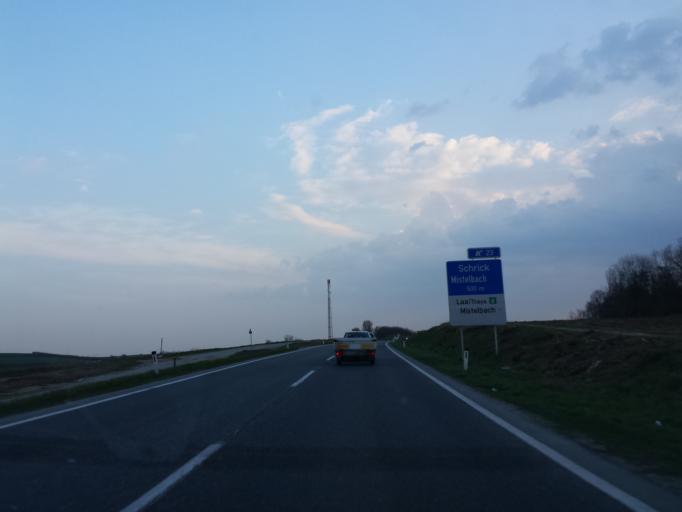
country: AT
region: Lower Austria
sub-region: Politischer Bezirk Mistelbach
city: Wilfersdorf
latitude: 48.5264
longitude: 16.6270
